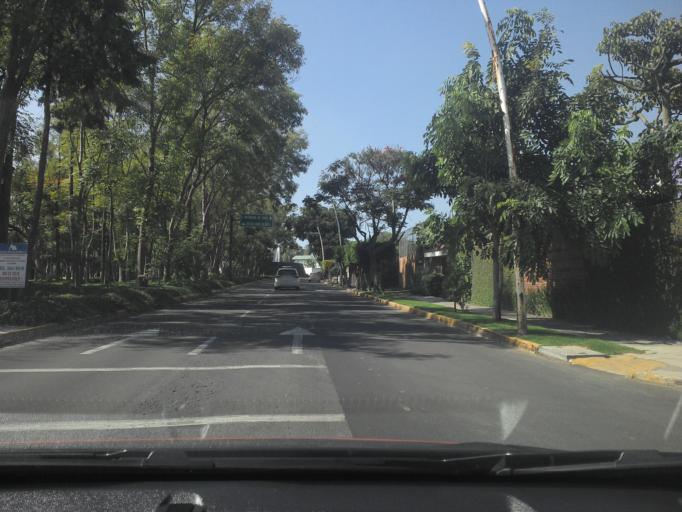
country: MX
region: Jalisco
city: Zapopan2
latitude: 20.6960
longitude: -103.3961
